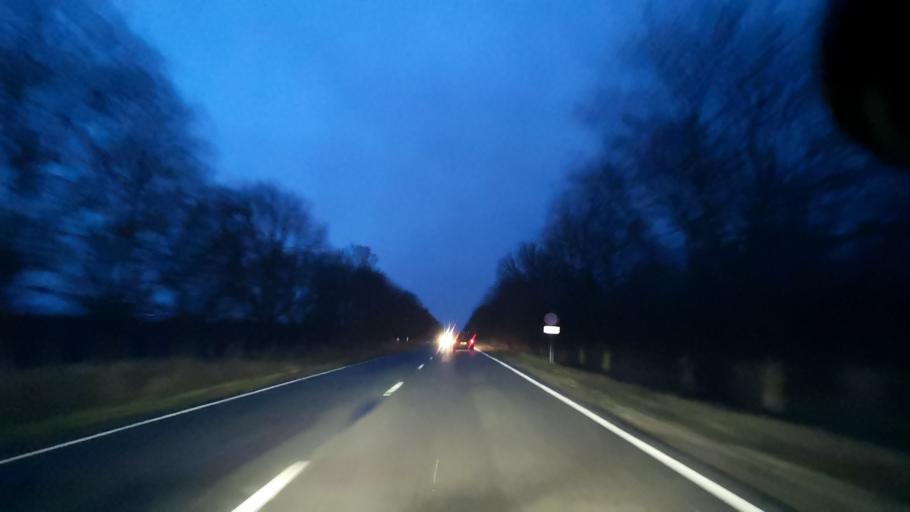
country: MD
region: Orhei
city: Orhei
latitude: 47.4670
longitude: 28.7913
